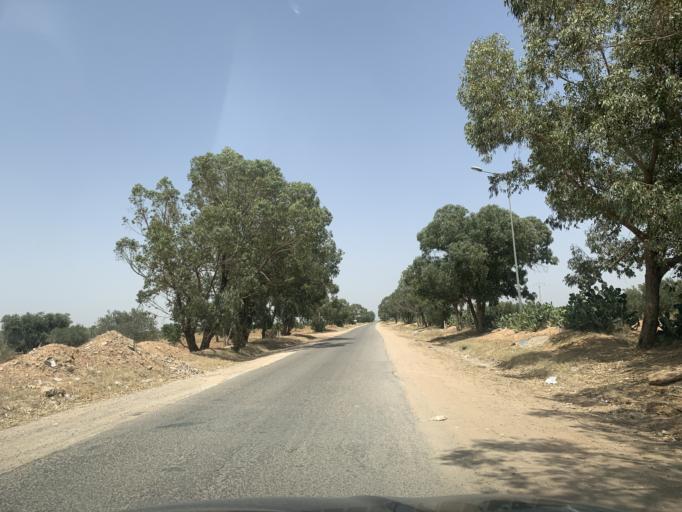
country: TN
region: Al Mahdiyah
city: Shurban
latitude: 35.1727
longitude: 10.2298
